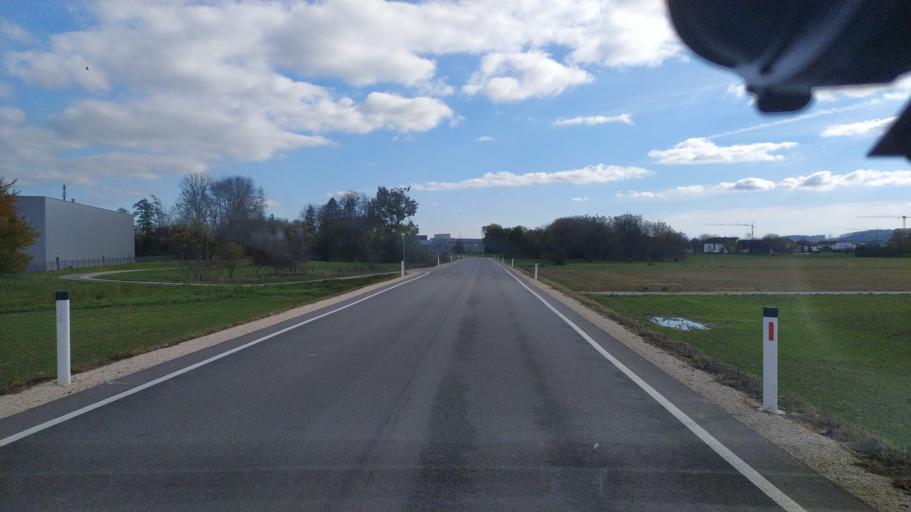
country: AT
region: Upper Austria
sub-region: Politischer Bezirk Urfahr-Umgebung
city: Steyregg
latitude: 48.2532
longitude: 14.3750
